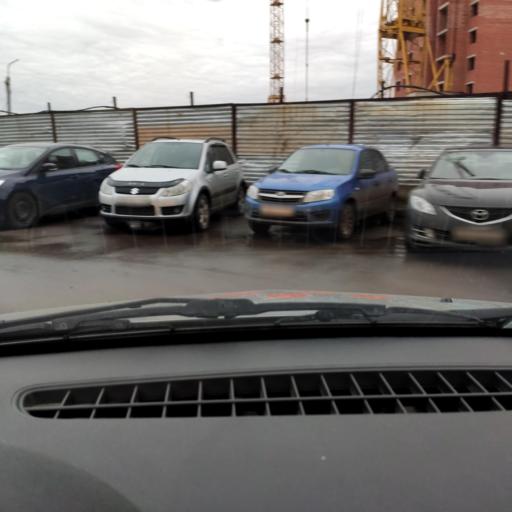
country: RU
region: Bashkortostan
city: Mikhaylovka
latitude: 54.7108
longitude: 55.8413
